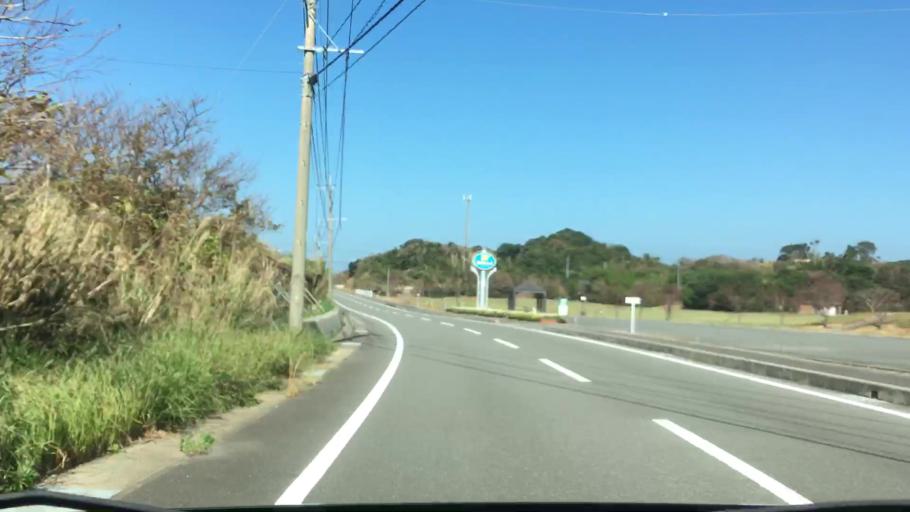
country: JP
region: Nagasaki
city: Sasebo
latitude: 33.0156
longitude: 129.5734
